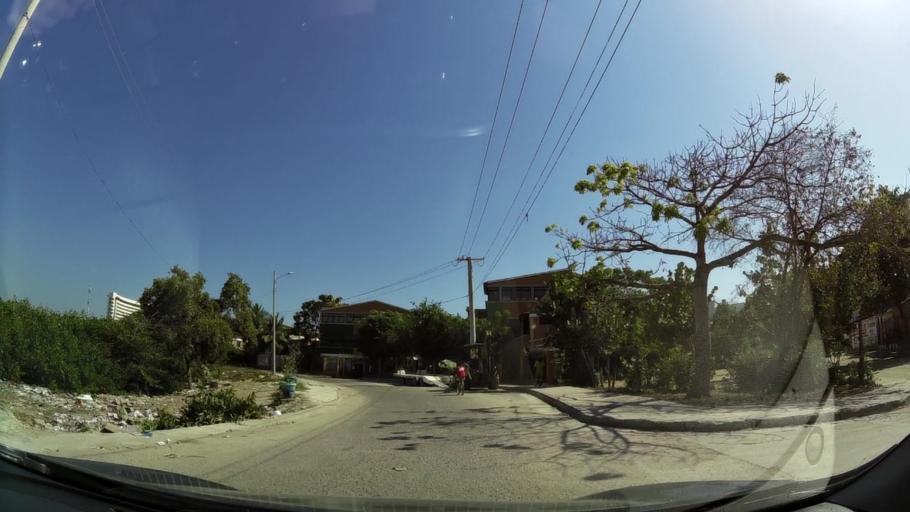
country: CO
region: Bolivar
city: Cartagena
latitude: 10.4391
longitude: -75.5267
